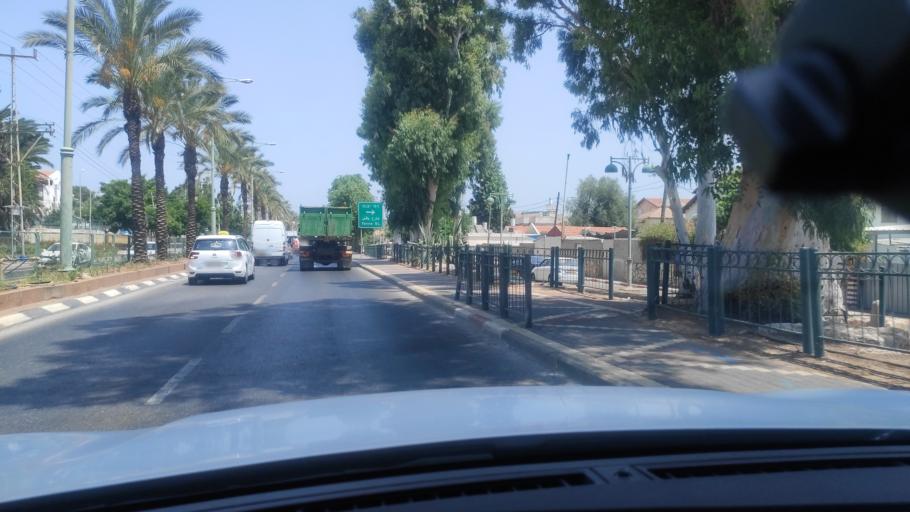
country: IL
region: Central District
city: Petah Tiqwa
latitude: 32.0926
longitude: 34.9023
